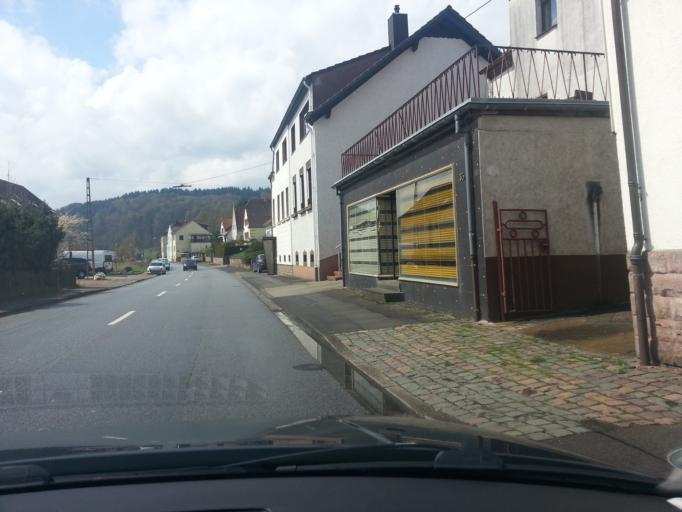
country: DE
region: Saarland
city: Blieskastel
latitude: 49.2627
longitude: 7.2799
